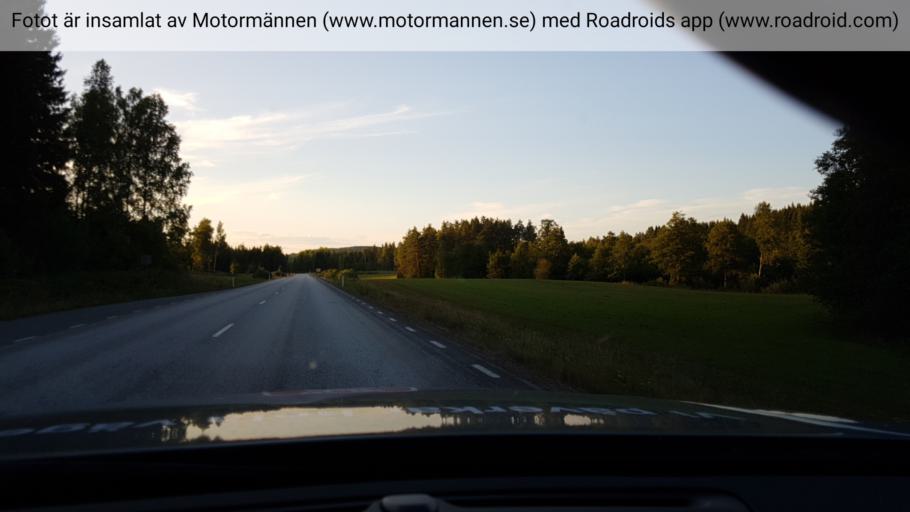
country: SE
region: Vaermland
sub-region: Storfors Kommun
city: Storfors
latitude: 59.4871
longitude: 14.3286
